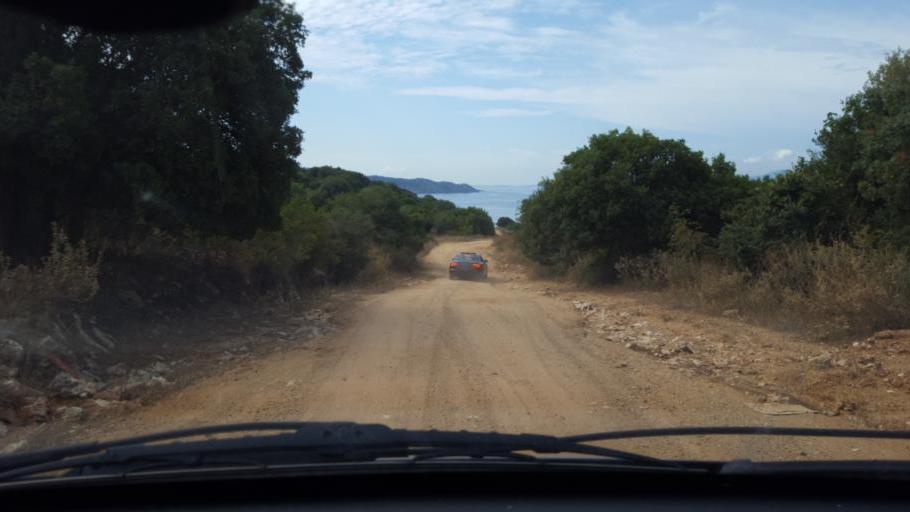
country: AL
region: Vlore
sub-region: Rrethi i Sarandes
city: Xarre
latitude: 39.7504
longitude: 19.9773
